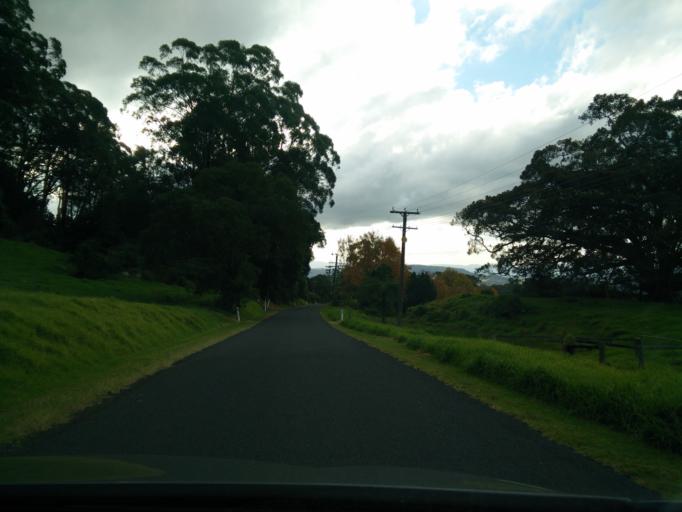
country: AU
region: New South Wales
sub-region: Kiama
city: Jamberoo
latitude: -34.6921
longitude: 150.7880
